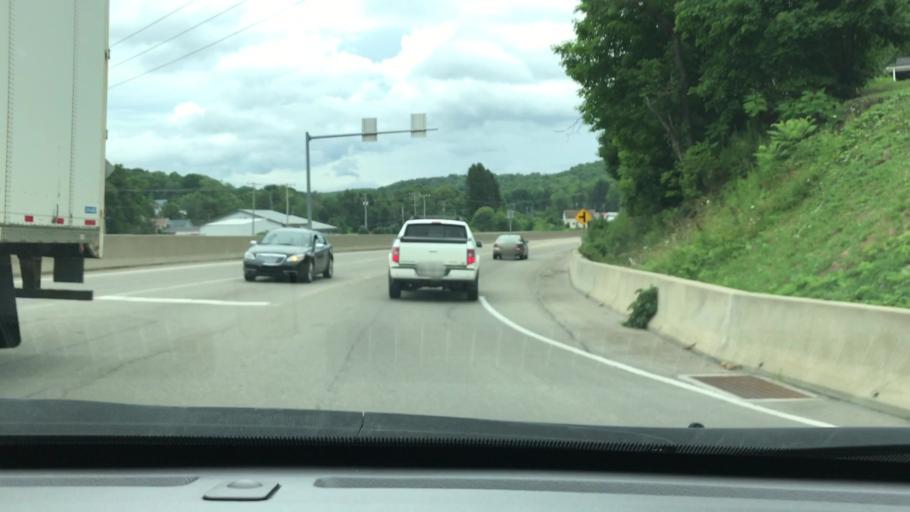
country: US
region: Pennsylvania
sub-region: Elk County
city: Johnsonburg
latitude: 41.4965
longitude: -78.6826
